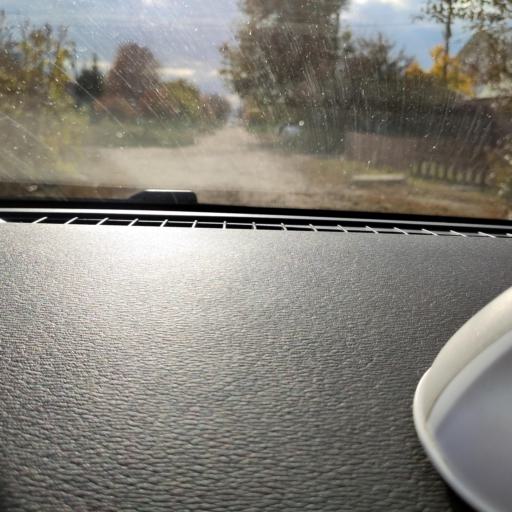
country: RU
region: Samara
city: Petra-Dubrava
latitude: 53.2477
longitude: 50.3142
